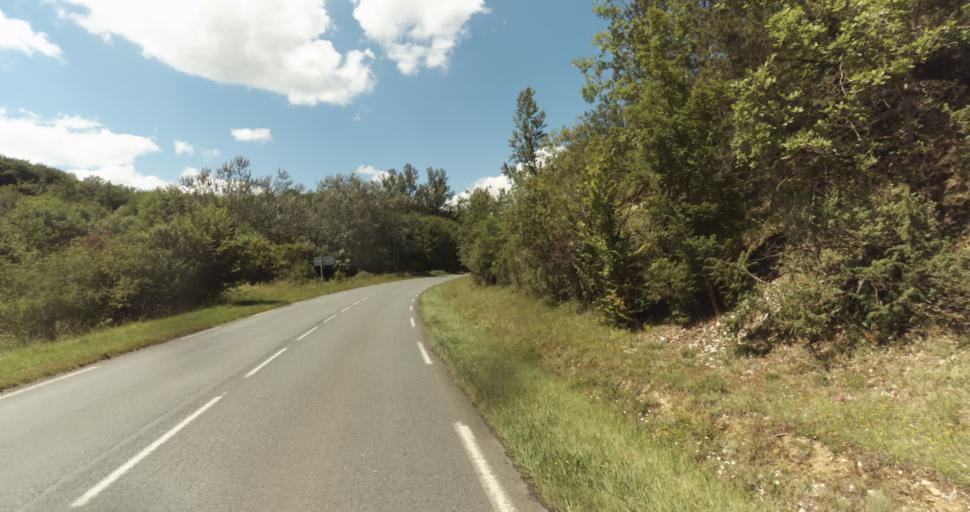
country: FR
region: Aquitaine
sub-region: Departement de la Dordogne
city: Lalinde
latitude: 44.8491
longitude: 0.8135
